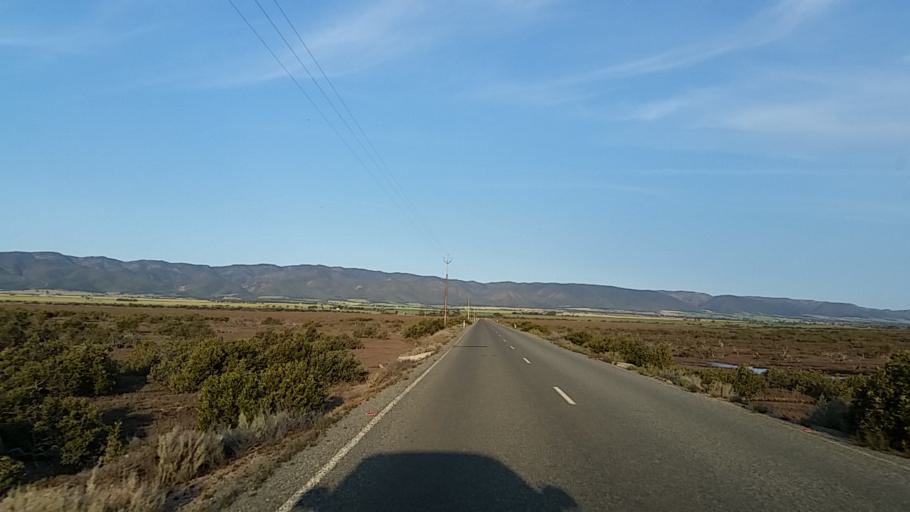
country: AU
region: South Australia
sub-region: Port Pirie City and Dists
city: Port Pirie
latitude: -33.1023
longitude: 138.0403
